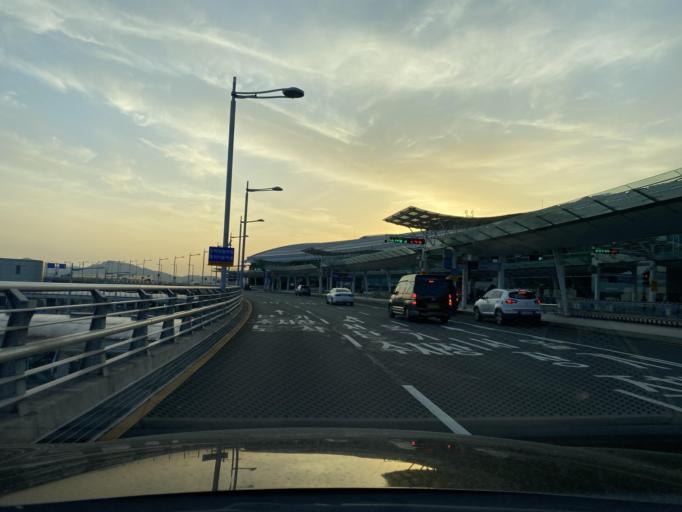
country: KR
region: Incheon
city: Incheon
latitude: 37.4486
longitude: 126.4516
